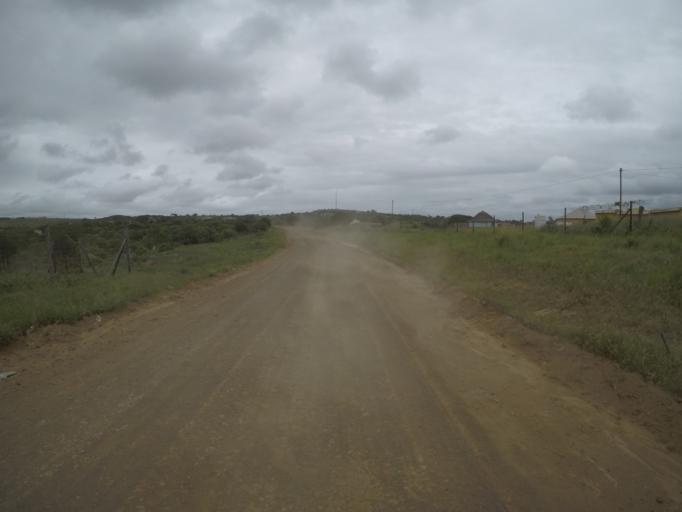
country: ZA
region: KwaZulu-Natal
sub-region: uThungulu District Municipality
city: Empangeni
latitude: -28.5970
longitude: 31.8382
